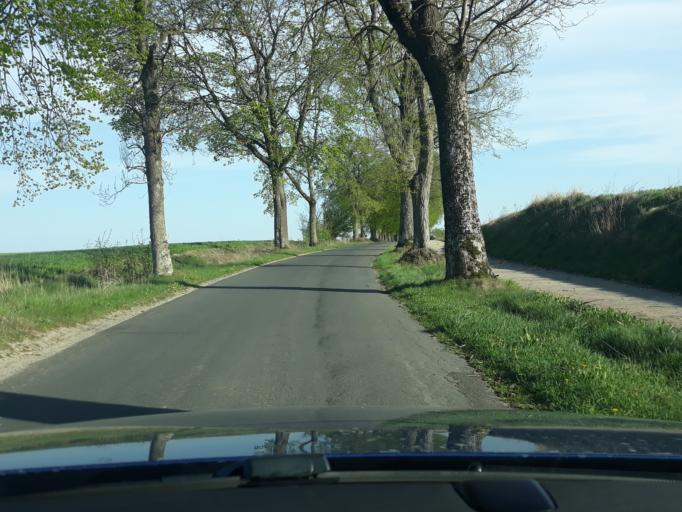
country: PL
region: Pomeranian Voivodeship
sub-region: Powiat czluchowski
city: Przechlewo
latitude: 53.8395
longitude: 17.3632
